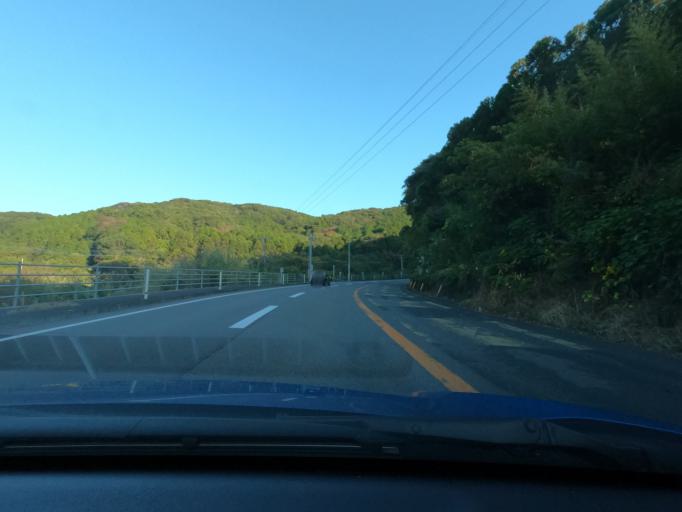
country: JP
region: Kagoshima
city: Akune
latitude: 31.9304
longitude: 130.2228
